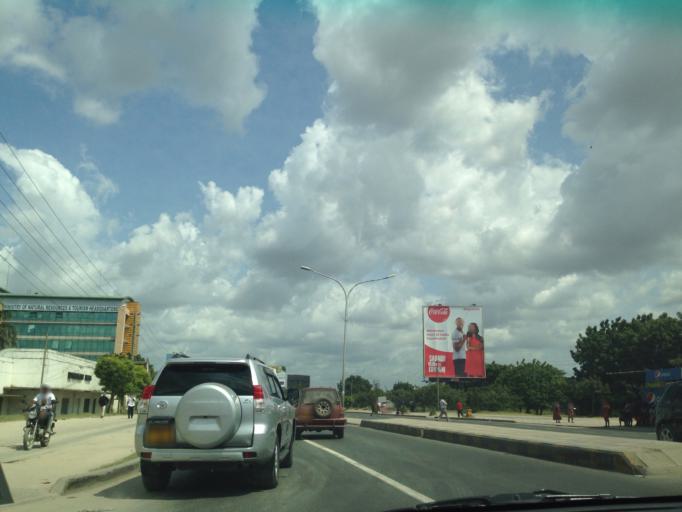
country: TZ
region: Dar es Salaam
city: Dar es Salaam
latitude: -6.8302
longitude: 39.2720
